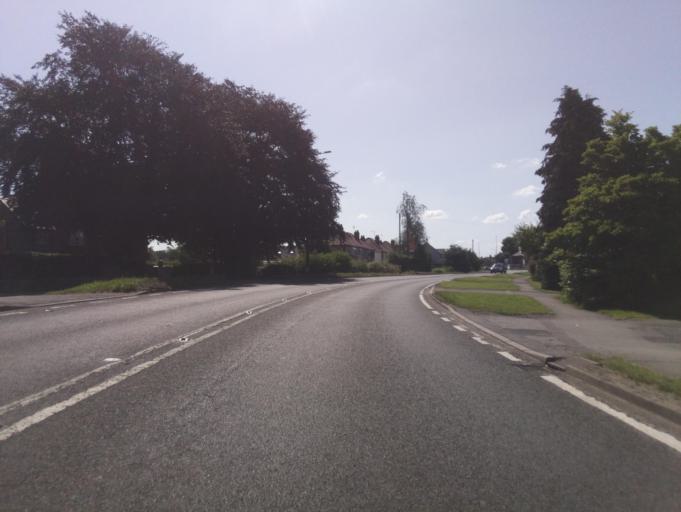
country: GB
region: England
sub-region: Derbyshire
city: Duffield
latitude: 52.9781
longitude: -1.4839
